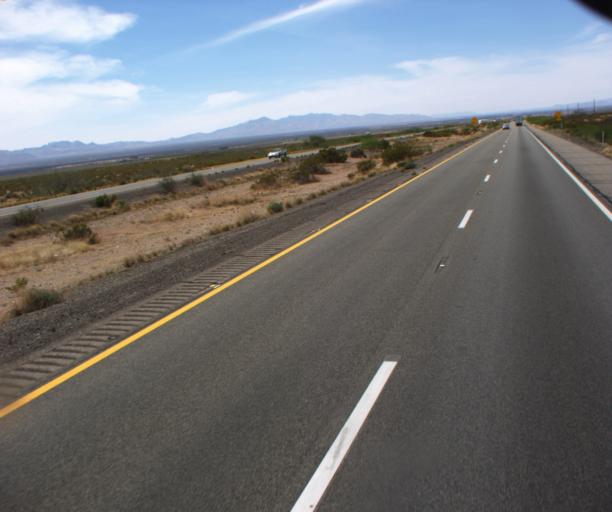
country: US
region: New Mexico
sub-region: Hidalgo County
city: Lordsburg
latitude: 32.2470
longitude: -109.1324
